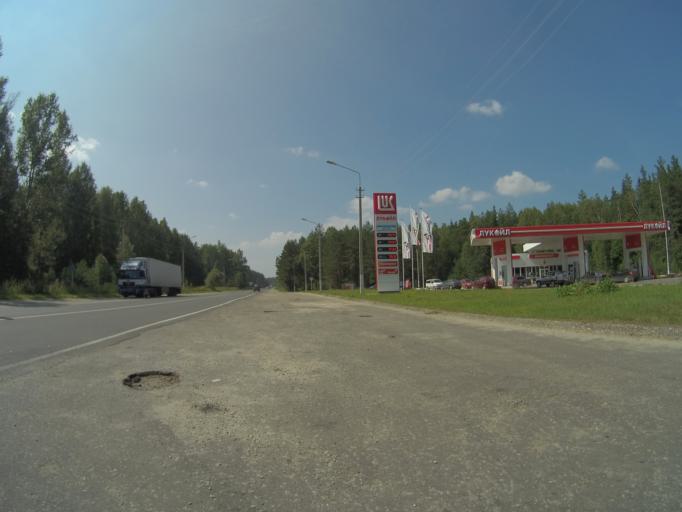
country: RU
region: Vladimir
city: Gus'-Khrustal'nyy
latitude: 55.6438
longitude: 40.7103
